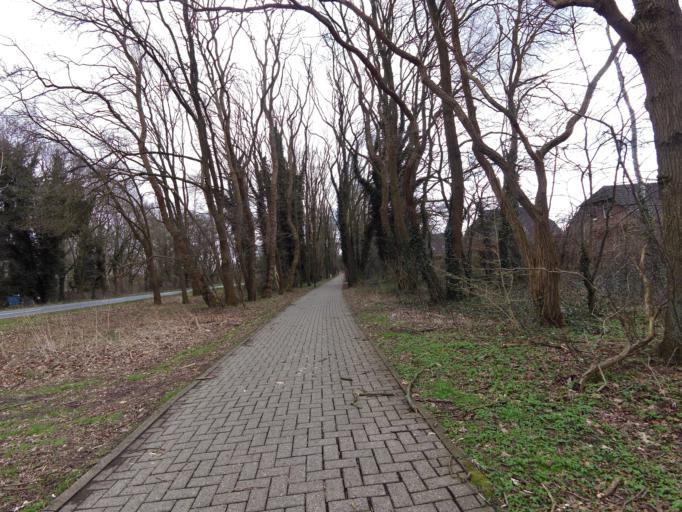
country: DE
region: Lower Saxony
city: Adelheidsdorf
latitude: 52.6040
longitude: 10.0286
